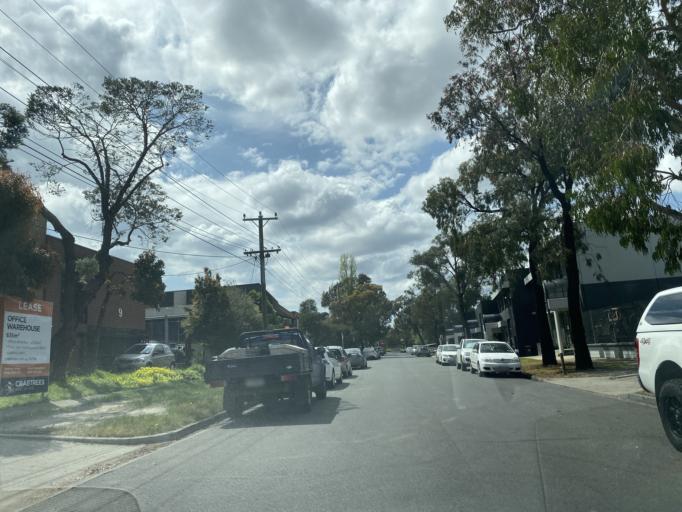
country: AU
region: Victoria
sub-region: Monash
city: Ashwood
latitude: -37.8538
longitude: 145.1036
